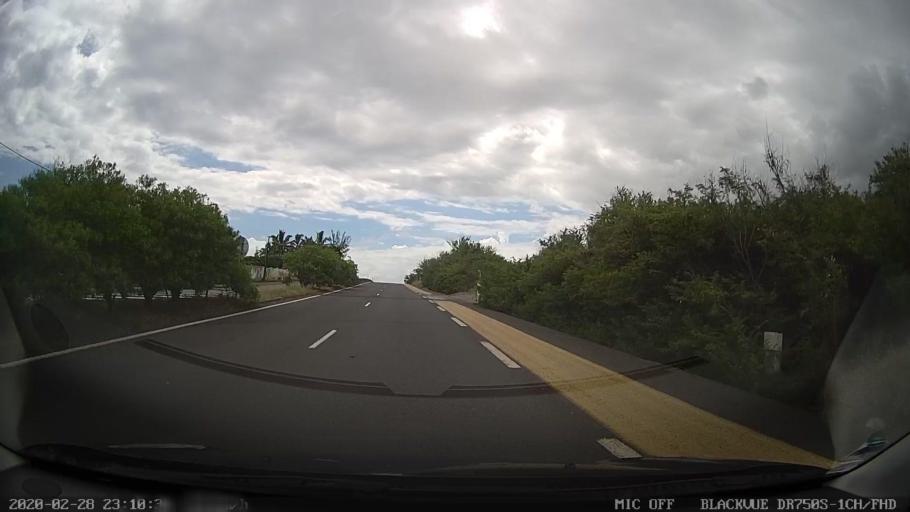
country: RE
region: Reunion
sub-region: Reunion
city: Trois-Bassins
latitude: -21.1171
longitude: 55.2594
